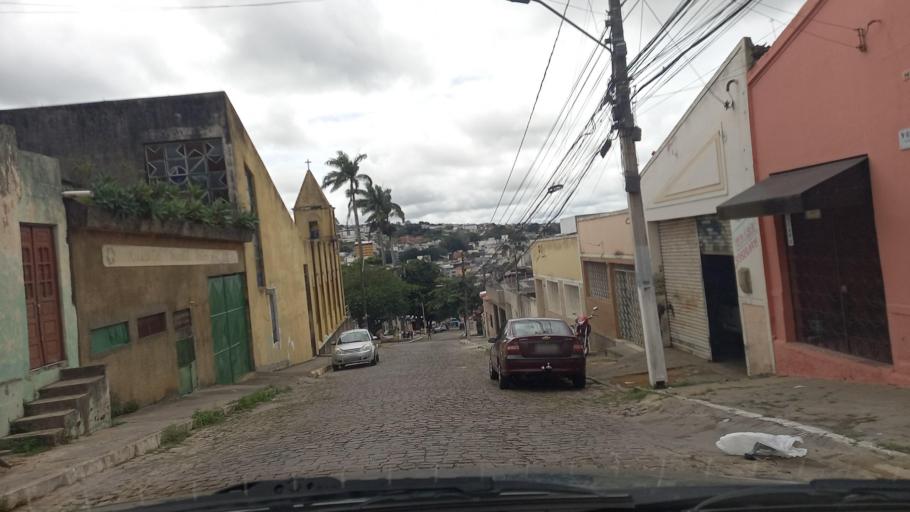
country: BR
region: Pernambuco
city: Garanhuns
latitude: -8.8978
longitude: -36.4951
